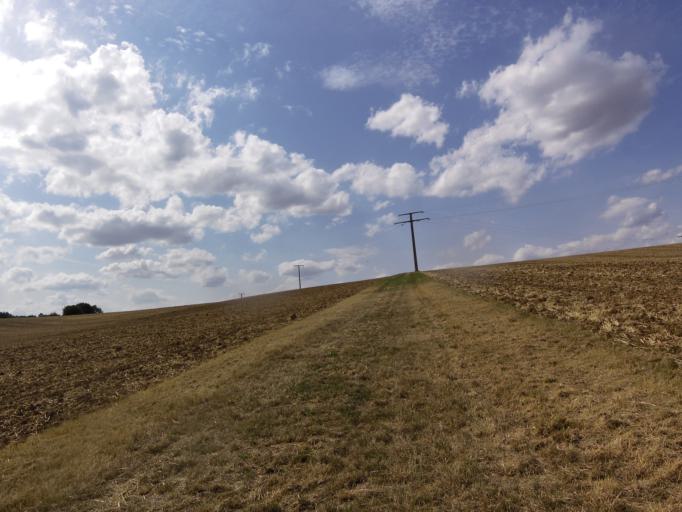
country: DE
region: Bavaria
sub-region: Regierungsbezirk Unterfranken
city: Waldbuttelbrunn
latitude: 49.7962
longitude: 9.8539
